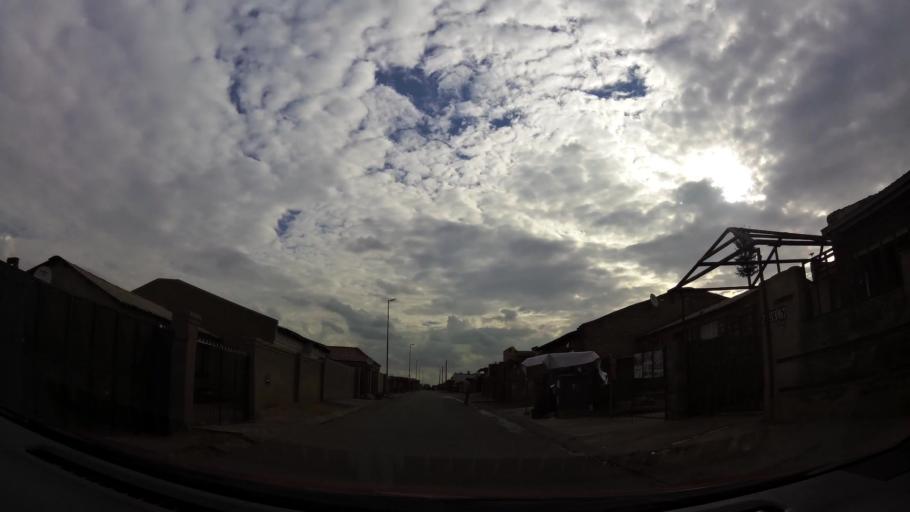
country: ZA
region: Gauteng
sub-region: City of Johannesburg Metropolitan Municipality
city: Soweto
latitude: -26.2467
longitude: 27.8360
